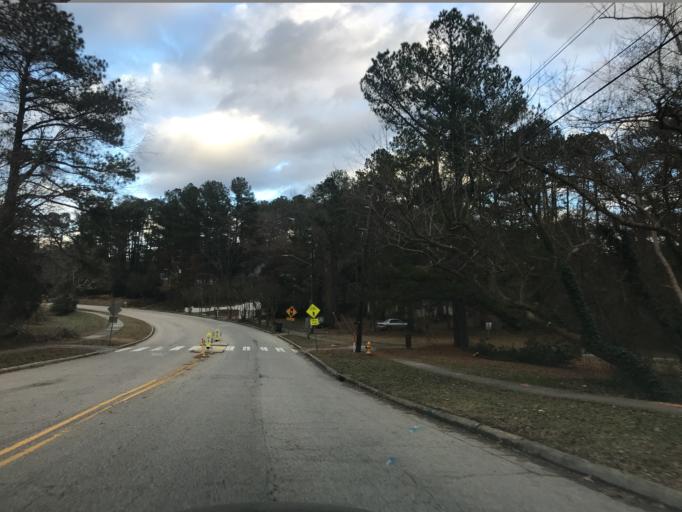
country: US
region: North Carolina
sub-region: Wake County
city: West Raleigh
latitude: 35.8423
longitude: -78.6623
